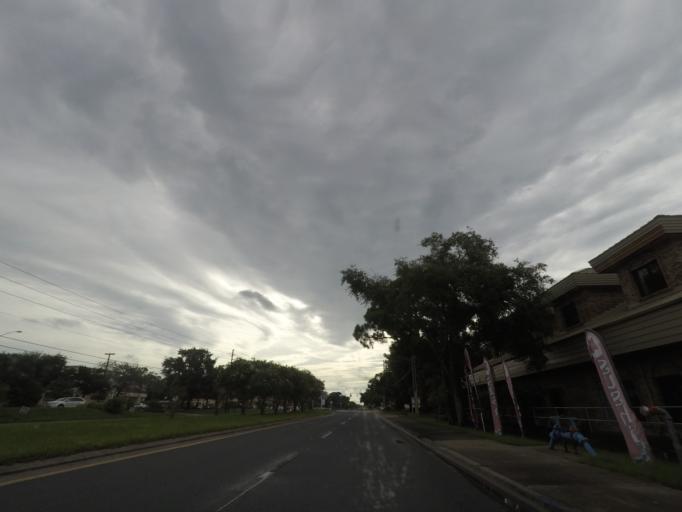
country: US
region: Florida
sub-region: Pinellas County
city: Redington Shores
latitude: 27.8437
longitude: -82.8297
